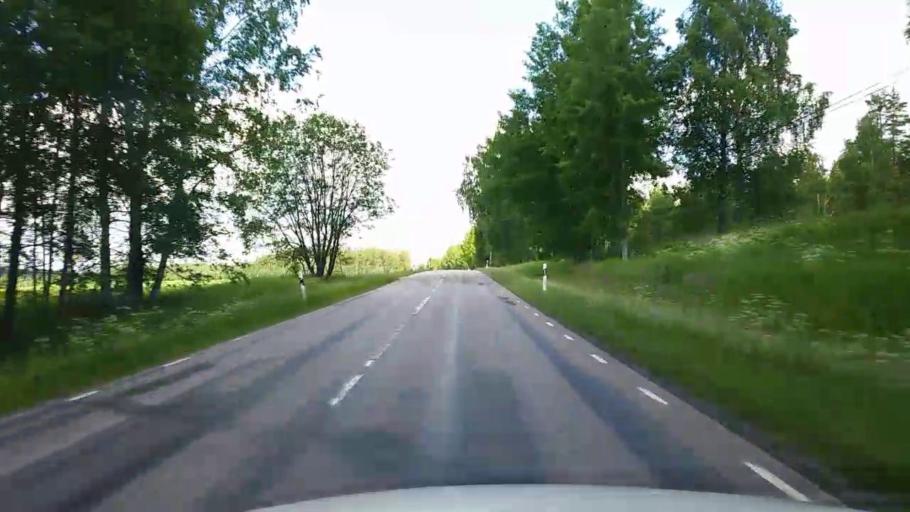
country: SE
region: Vaestmanland
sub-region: Kopings Kommun
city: Kolsva
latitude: 59.6752
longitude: 15.7680
